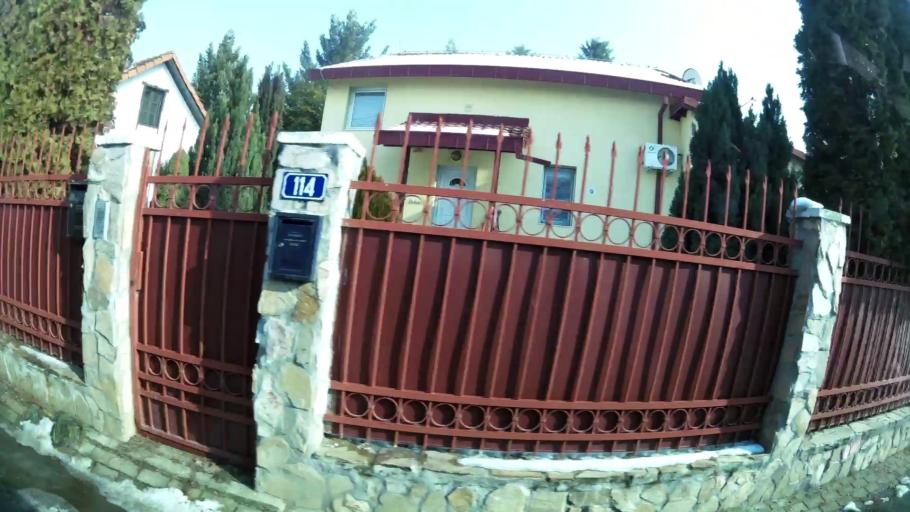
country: MK
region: Suto Orizari
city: Suto Orizare
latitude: 42.0257
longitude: 21.3881
